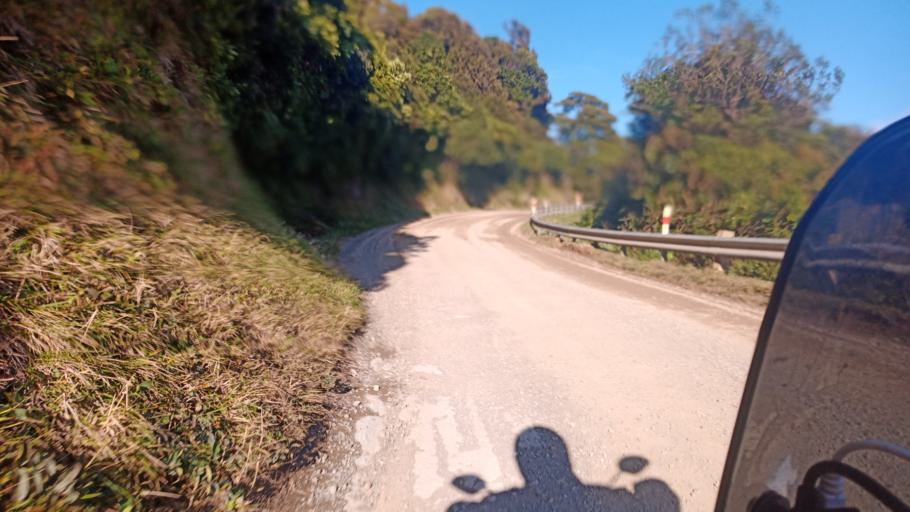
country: NZ
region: Hawke's Bay
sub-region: Wairoa District
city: Wairoa
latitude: -38.7882
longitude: 177.1291
